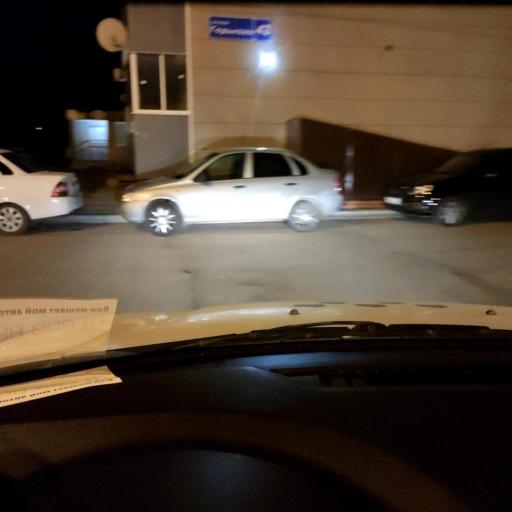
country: RU
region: Samara
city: Tol'yatti
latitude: 53.5220
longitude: 49.4189
